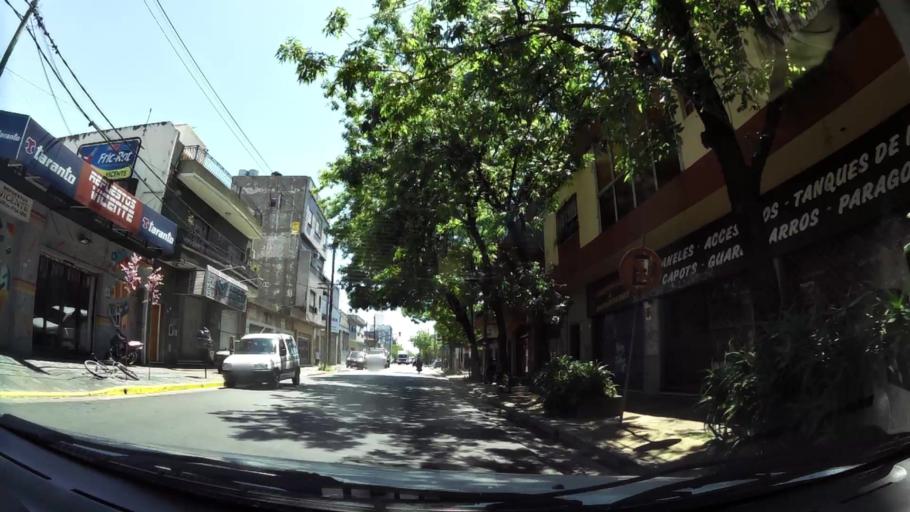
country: AR
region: Buenos Aires
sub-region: Partido de General San Martin
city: General San Martin
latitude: -34.5517
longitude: -58.5306
